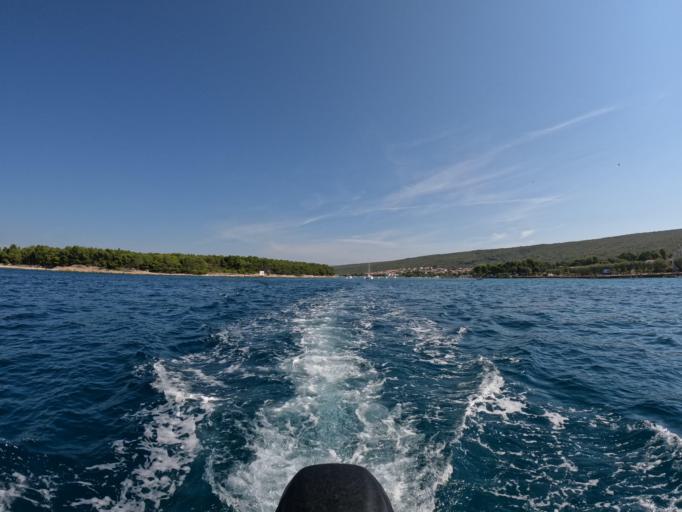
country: HR
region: Primorsko-Goranska
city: Punat
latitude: 45.0118
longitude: 14.6208
